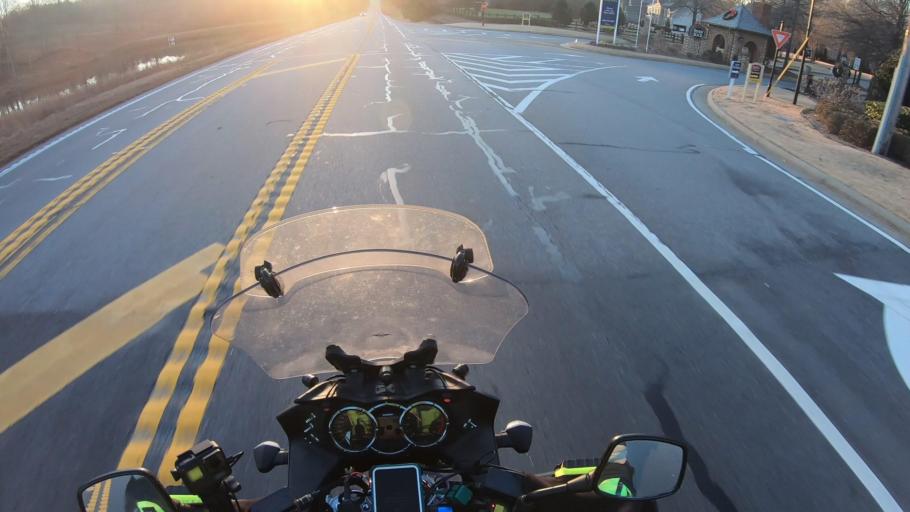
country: US
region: Georgia
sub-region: Forsyth County
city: Cumming
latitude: 34.2994
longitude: -84.2310
